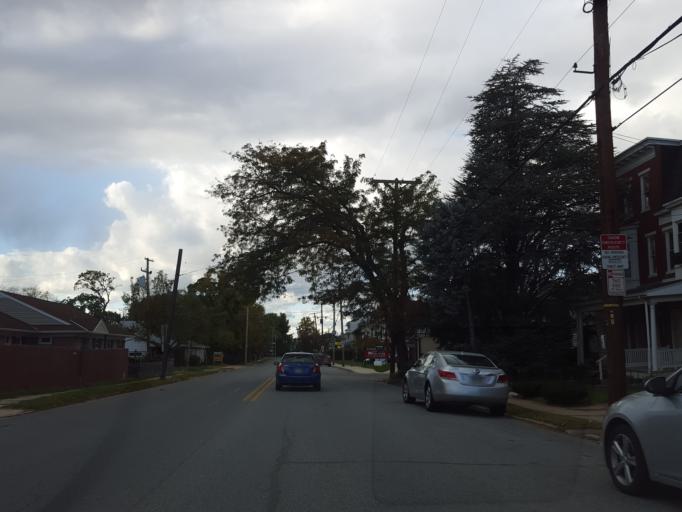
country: US
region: Pennsylvania
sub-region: York County
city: Valley View
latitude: 39.9505
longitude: -76.7146
